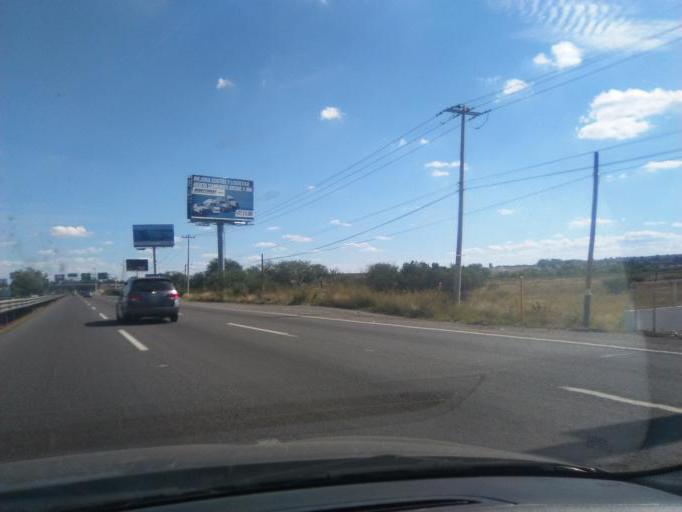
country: MX
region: Guanajuato
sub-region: Silao de la Victoria
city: El Refugio de los Sauces
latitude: 21.0030
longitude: -101.5123
